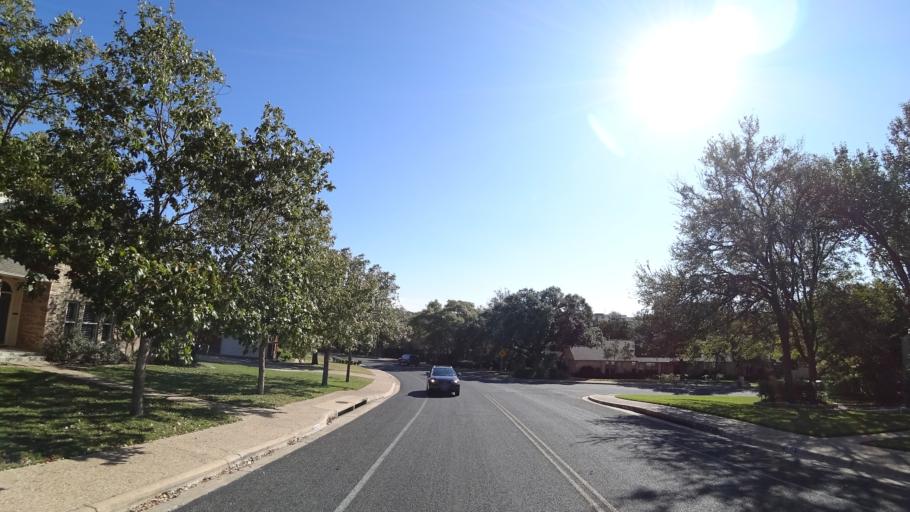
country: US
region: Texas
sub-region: Williamson County
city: Jollyville
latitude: 30.4072
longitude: -97.7562
